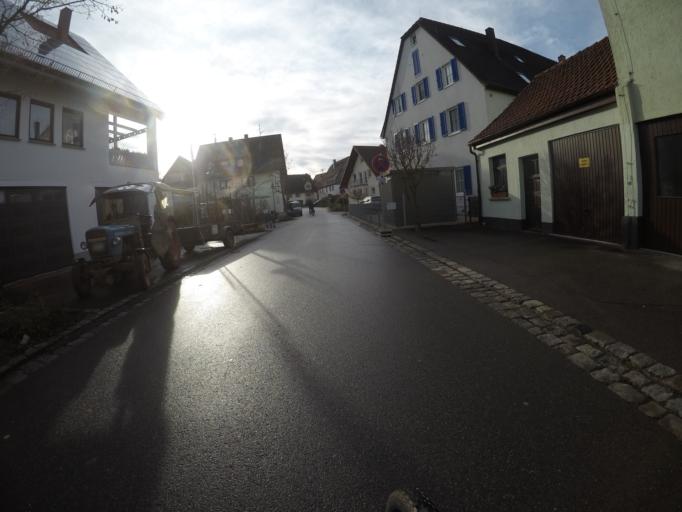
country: DE
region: Baden-Wuerttemberg
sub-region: Regierungsbezirk Stuttgart
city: Deckenpfronn
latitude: 48.6518
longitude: 8.8210
